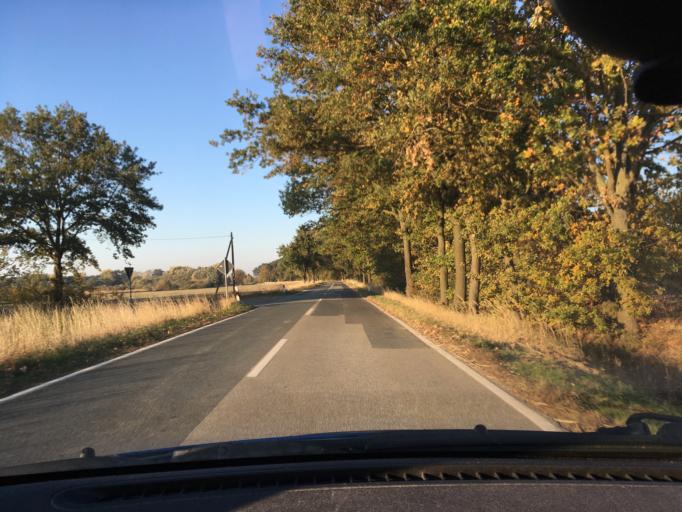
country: DE
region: Lower Saxony
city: Bleckede
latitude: 53.3116
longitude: 10.7913
